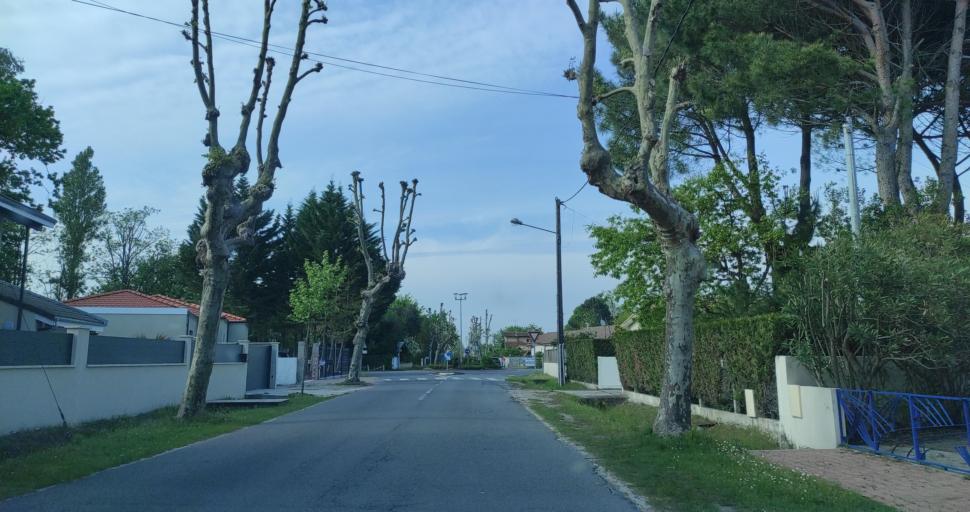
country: FR
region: Aquitaine
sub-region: Departement de la Gironde
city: Ares
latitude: 44.7602
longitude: -1.1328
